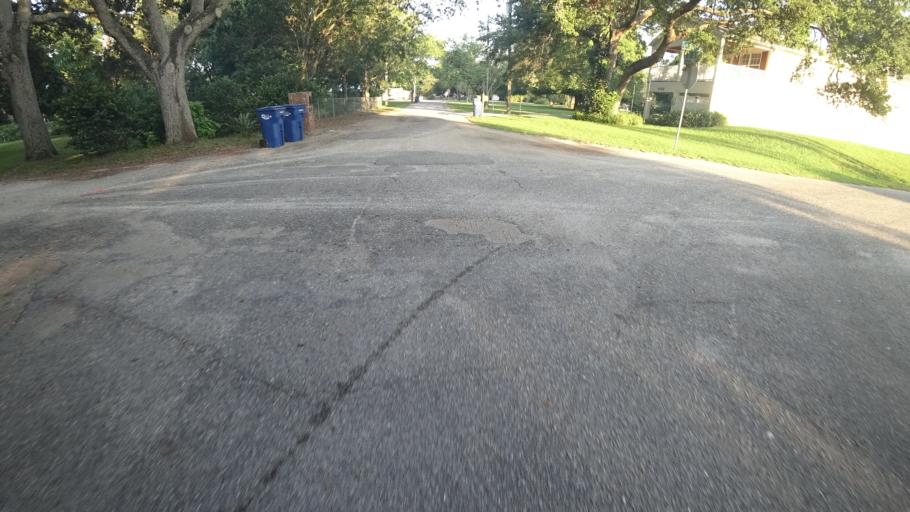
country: US
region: Florida
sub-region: Manatee County
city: West Bradenton
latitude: 27.5197
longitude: -82.6007
